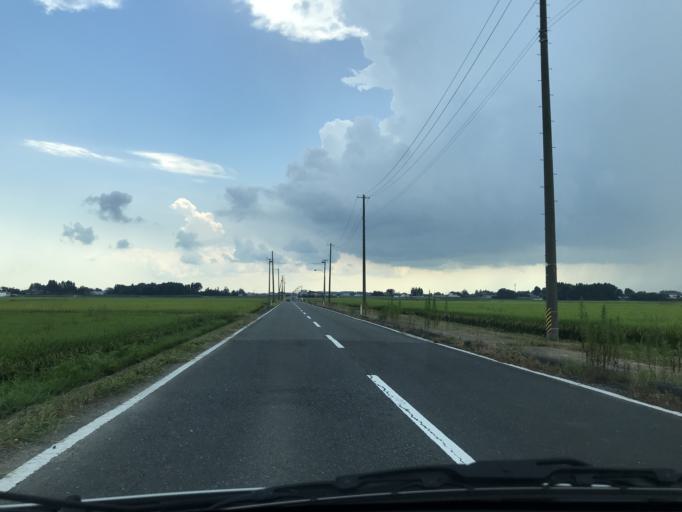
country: JP
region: Iwate
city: Ichinoseki
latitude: 38.7713
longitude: 141.0688
